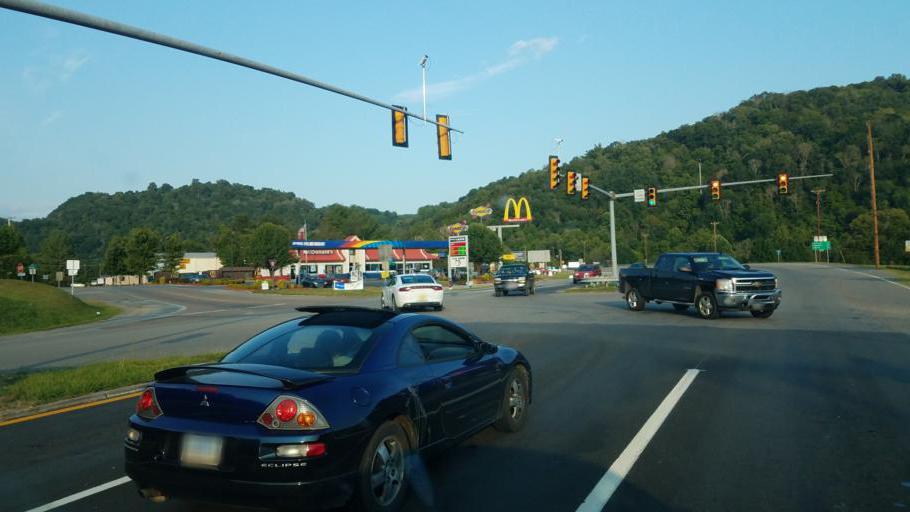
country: US
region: Virginia
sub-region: Lee County
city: Dryden
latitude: 36.7118
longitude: -82.7929
